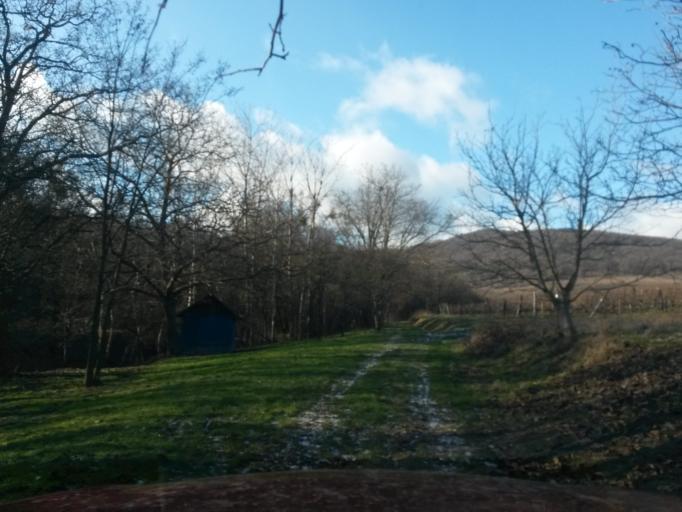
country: HU
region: Borsod-Abauj-Zemplen
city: Sarospatak
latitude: 48.3301
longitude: 21.5216
